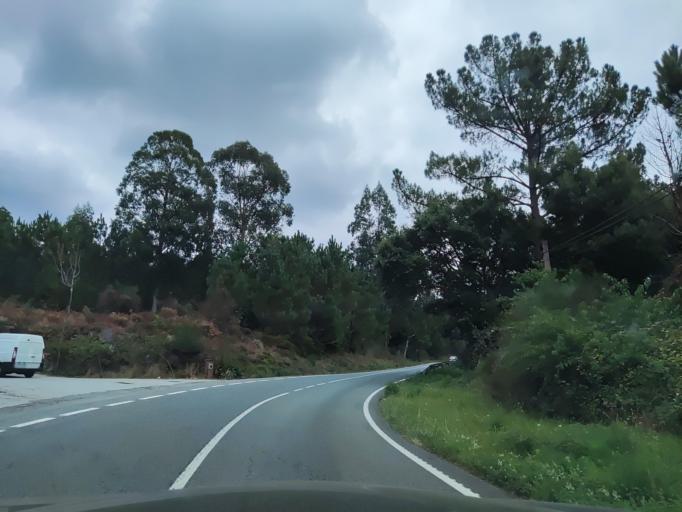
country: ES
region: Galicia
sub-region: Provincia da Coruna
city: Padron
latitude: 42.7390
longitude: -8.6297
